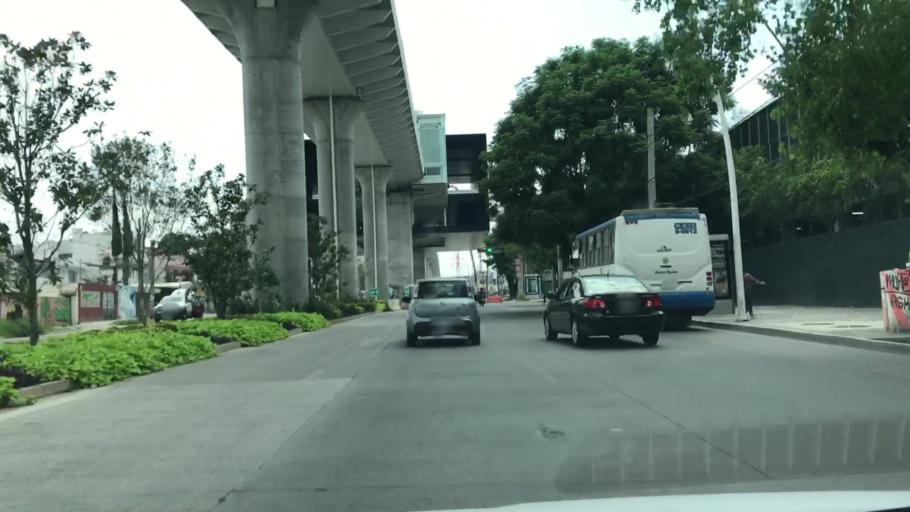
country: MX
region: Jalisco
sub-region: Zapopan
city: Zapopan
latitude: 20.7073
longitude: -103.3673
